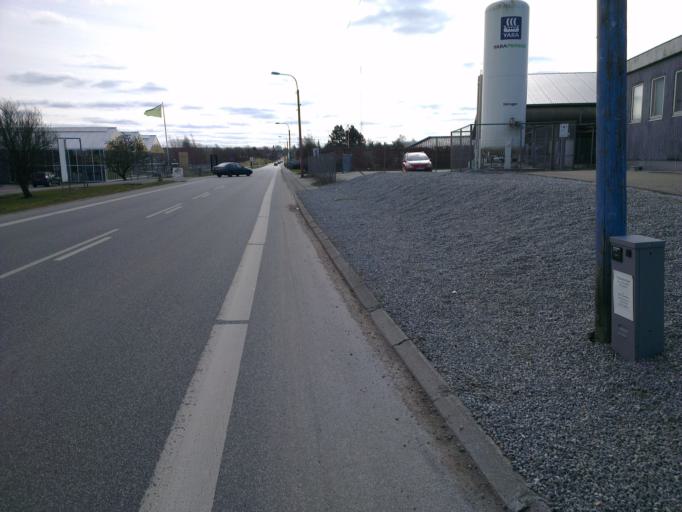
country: DK
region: Capital Region
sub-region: Frederikssund Kommune
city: Skibby
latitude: 55.7602
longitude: 11.9571
